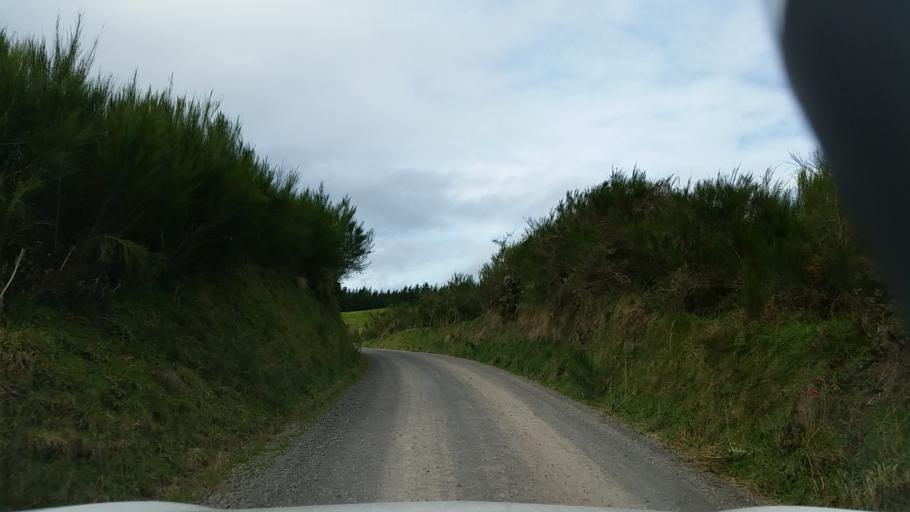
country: NZ
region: Bay of Plenty
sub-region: Whakatane District
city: Murupara
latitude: -38.3417
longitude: 176.5409
